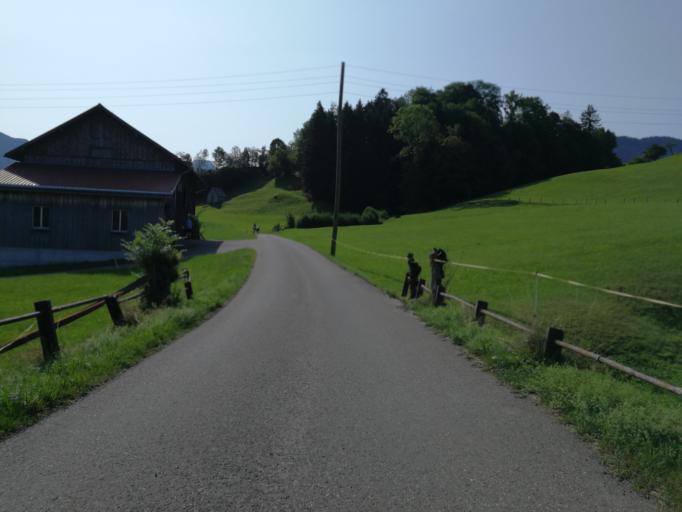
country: CH
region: Saint Gallen
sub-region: Wahlkreis Toggenburg
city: Krummenau
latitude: 47.2385
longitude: 9.1767
